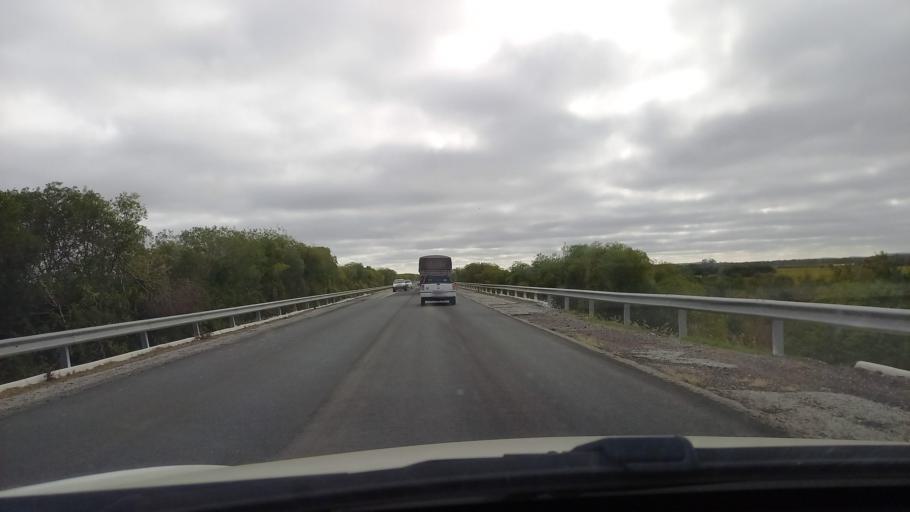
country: BR
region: Rio Grande do Sul
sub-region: Dom Pedrito
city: Dom Pedrito
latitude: -30.9472
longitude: -54.7146
